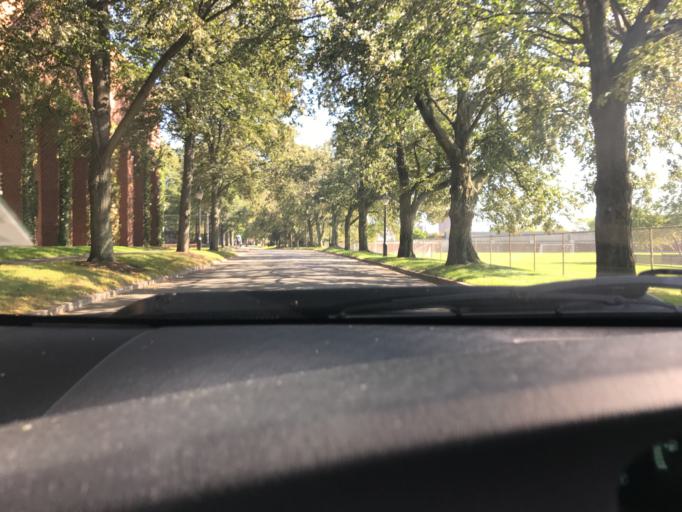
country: US
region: Massachusetts
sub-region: Middlesex County
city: Cambridge
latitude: 42.3662
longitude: -71.1252
